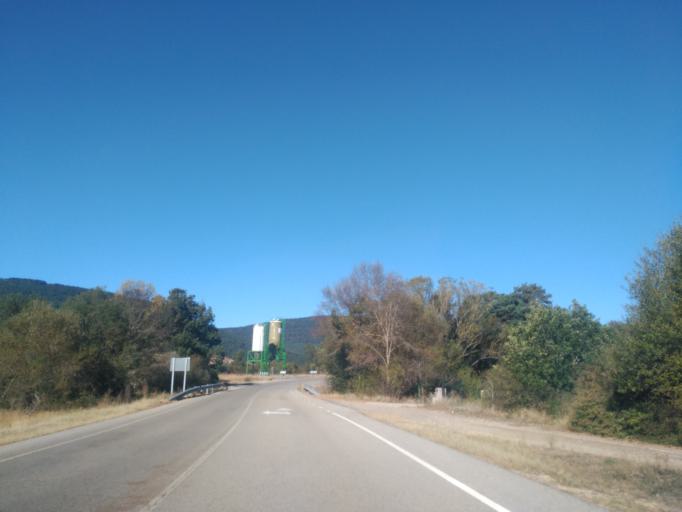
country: ES
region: Castille and Leon
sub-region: Provincia de Soria
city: Vinuesa
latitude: 41.9091
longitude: -2.7492
